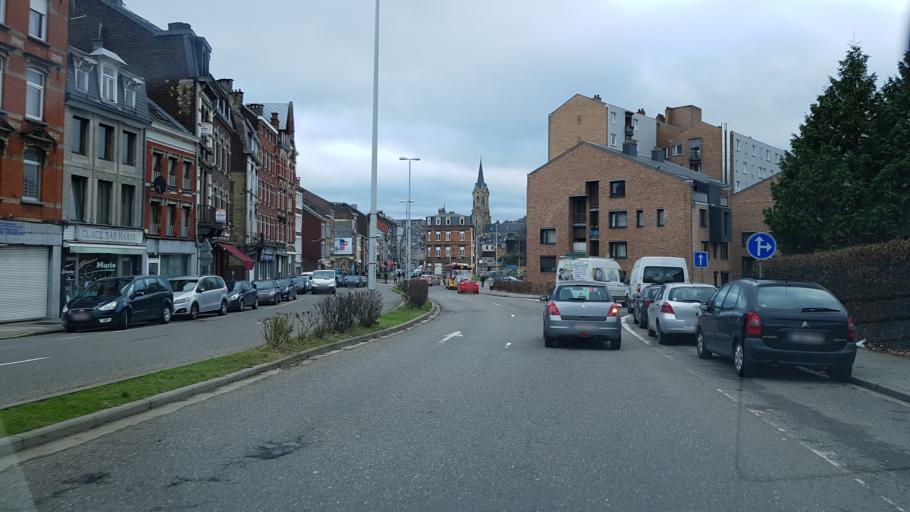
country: BE
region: Wallonia
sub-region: Province de Liege
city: Verviers
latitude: 50.5956
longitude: 5.8523
